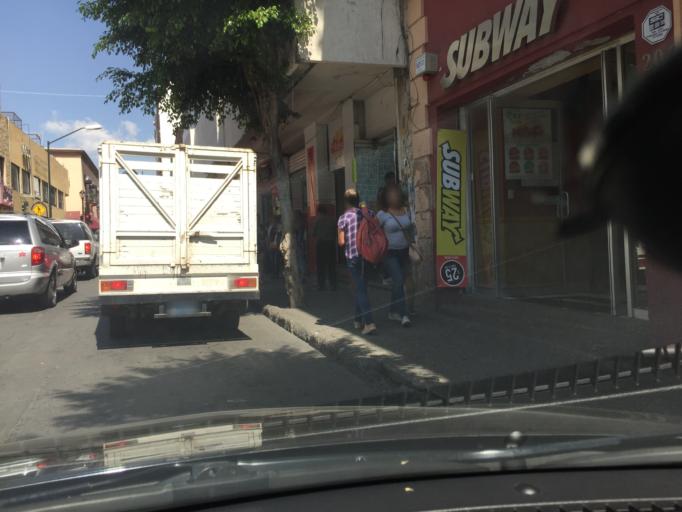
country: MX
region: Guanajuato
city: Leon
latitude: 21.1205
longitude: -101.6826
